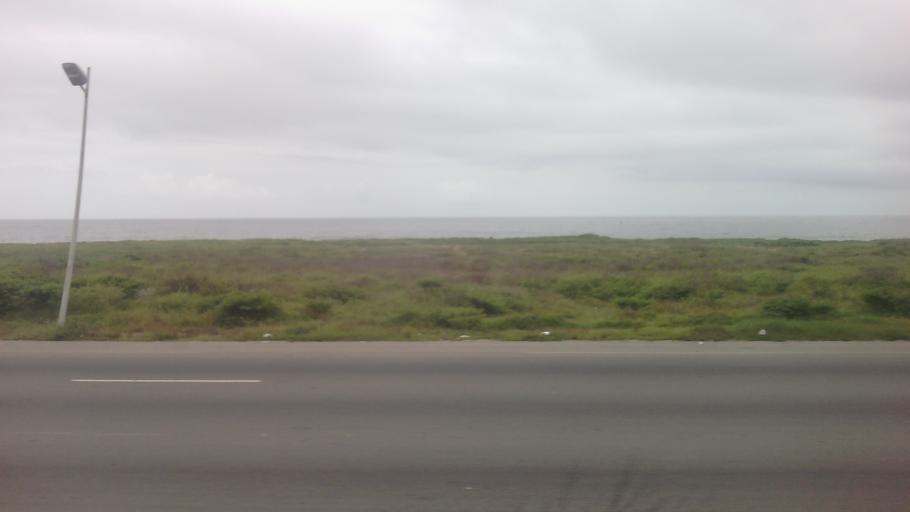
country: CI
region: Lagunes
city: Abidjan
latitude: 5.2451
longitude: -3.9325
